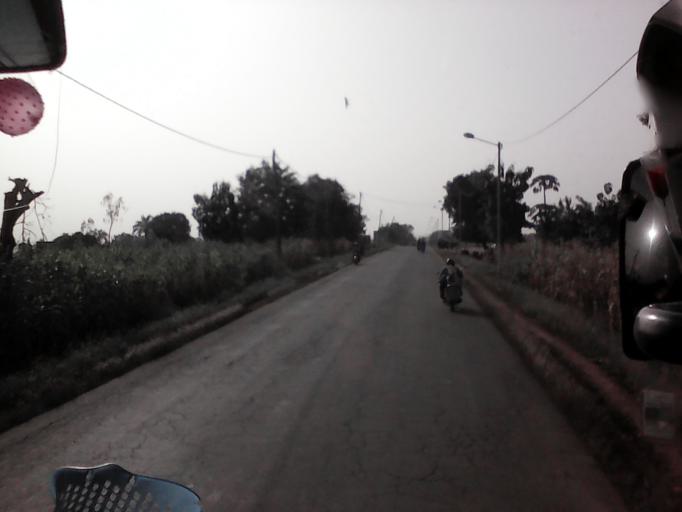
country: TG
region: Kara
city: Kara
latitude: 9.5277
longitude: 1.2046
